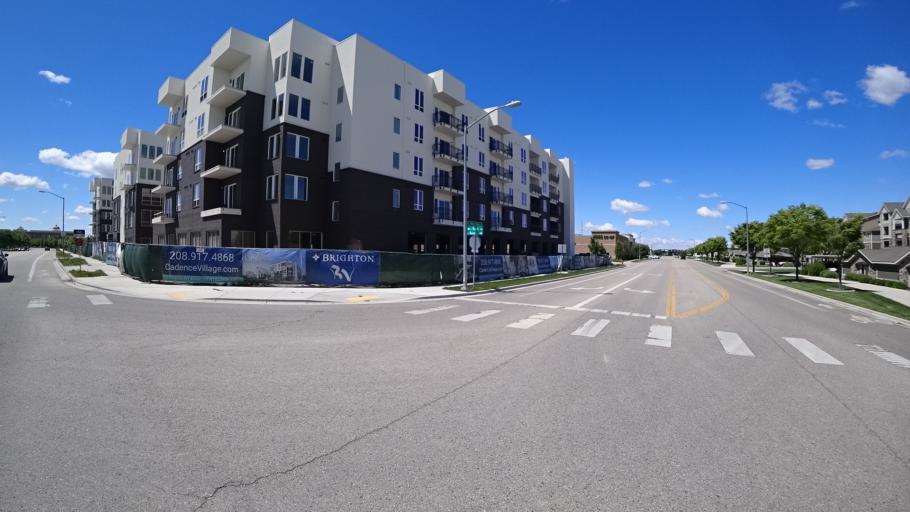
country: US
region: Idaho
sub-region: Ada County
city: Meridian
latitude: 43.6266
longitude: -116.3498
